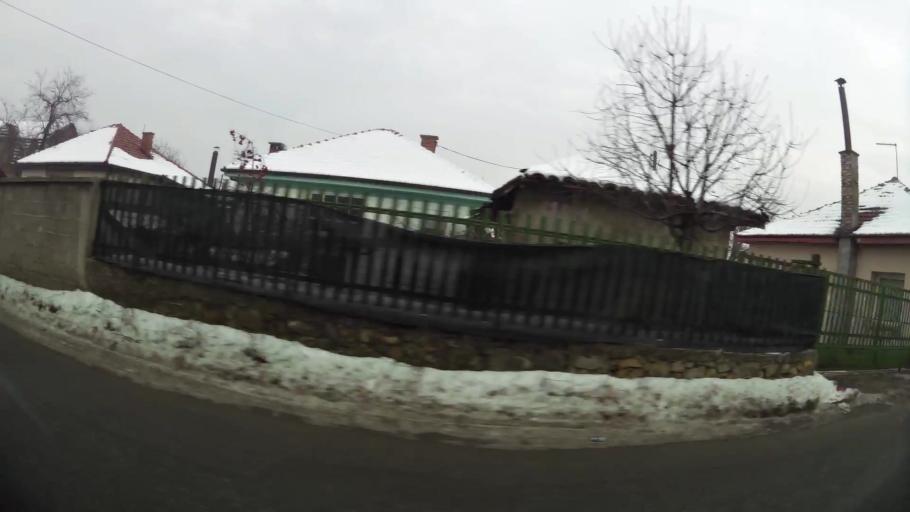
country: MK
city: Kondovo
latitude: 42.0455
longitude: 21.3485
